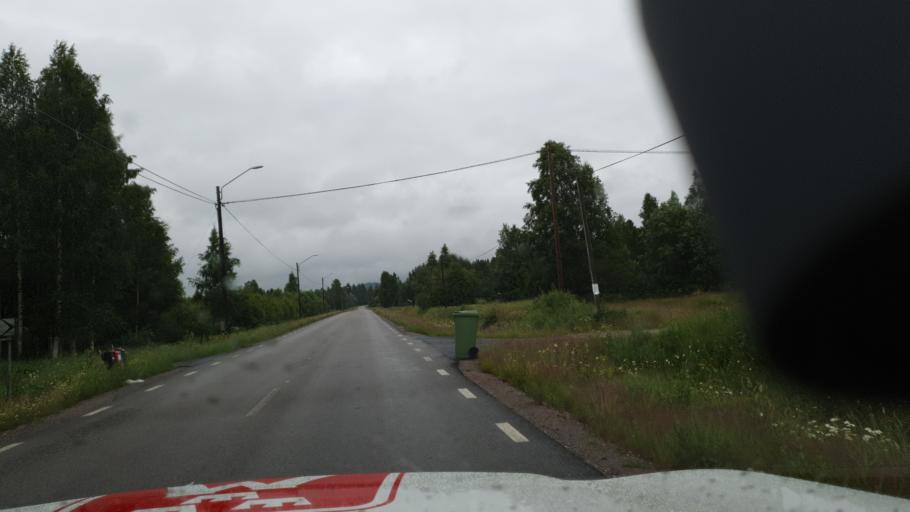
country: SE
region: Vaesterbotten
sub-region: Vannas Kommun
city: Vannasby
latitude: 63.7933
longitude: 19.8558
